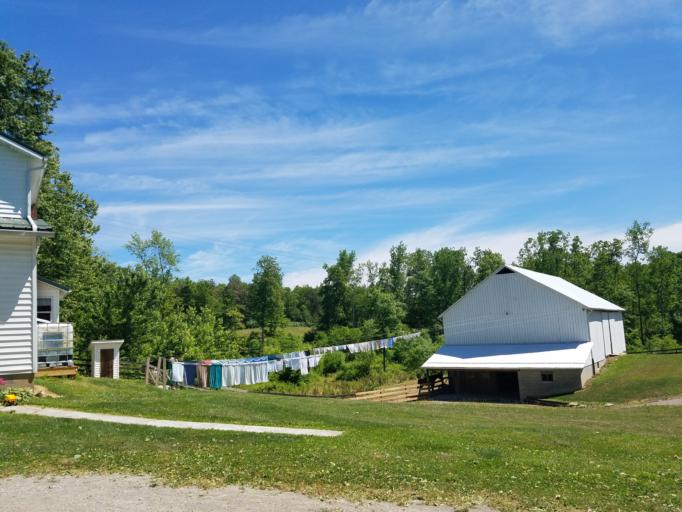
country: US
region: Ohio
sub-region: Columbiana County
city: Salineville
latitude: 40.5226
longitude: -80.8292
